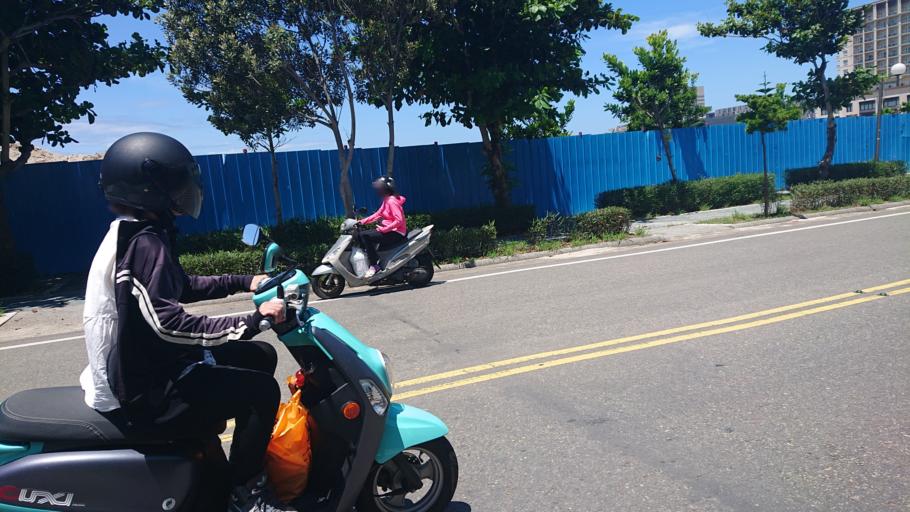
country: TW
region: Taiwan
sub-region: Penghu
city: Ma-kung
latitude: 23.5673
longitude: 119.5788
